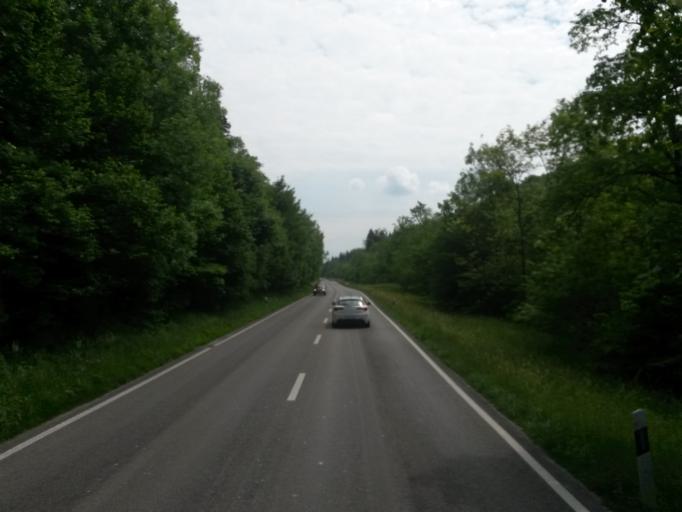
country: CH
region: Zurich
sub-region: Bezirk Pfaeffikon
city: Effretikon / Watt
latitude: 47.4301
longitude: 8.7069
